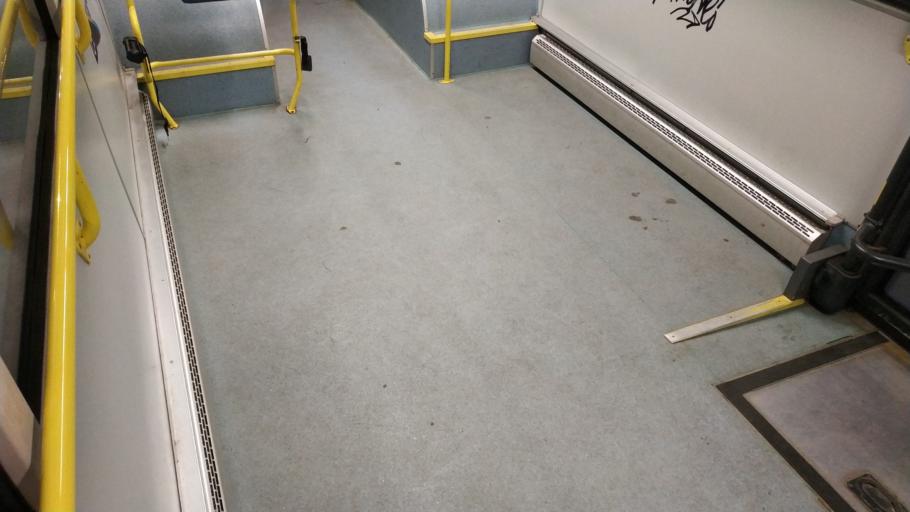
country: RU
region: Primorskiy
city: Russkiy
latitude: 43.0233
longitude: 131.8986
